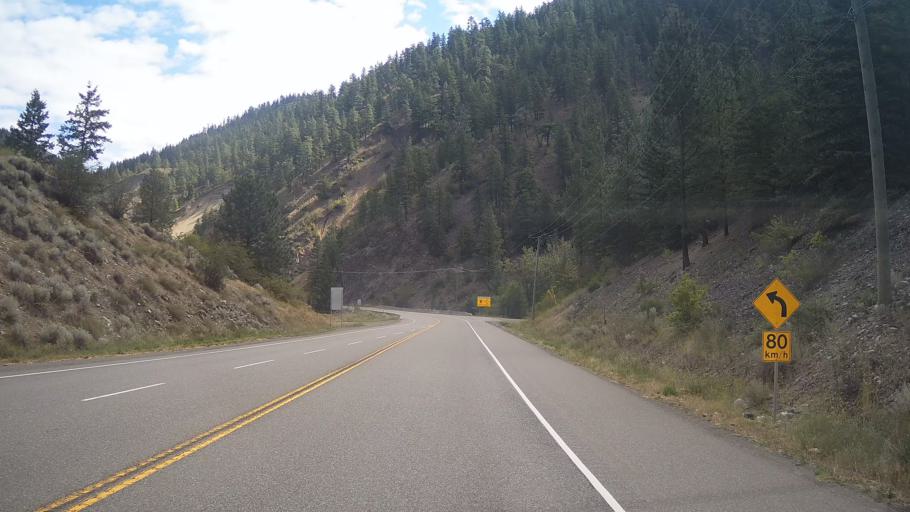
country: CA
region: British Columbia
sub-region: Thompson-Nicola Regional District
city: Ashcroft
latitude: 50.2478
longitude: -121.4804
